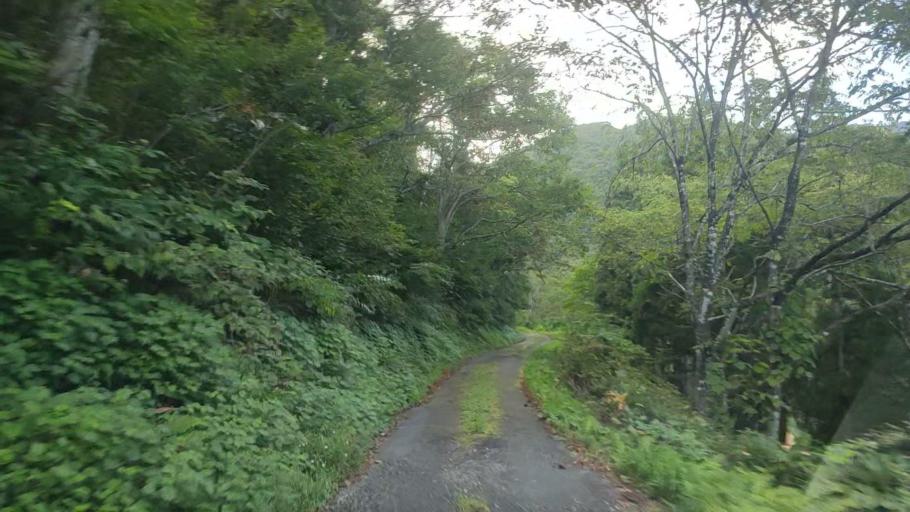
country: JP
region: Toyama
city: Yatsuomachi-higashikumisaka
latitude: 36.3269
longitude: 137.0792
